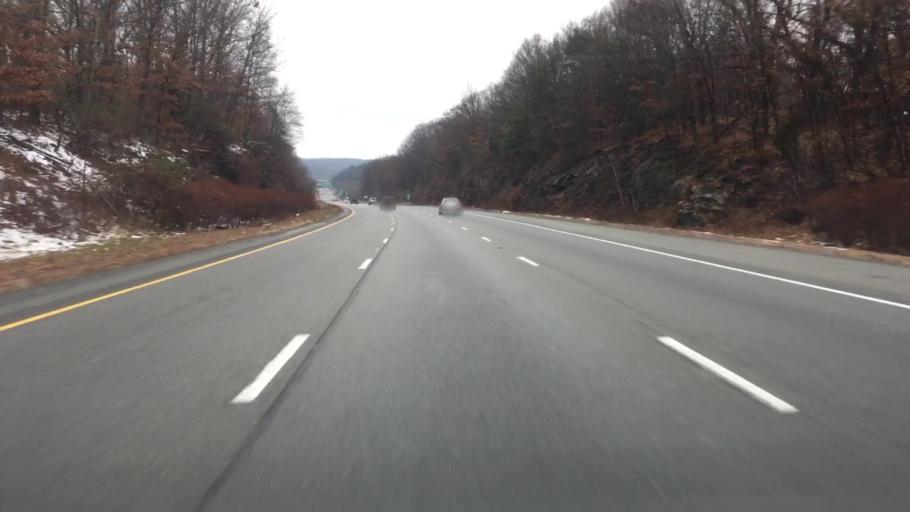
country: US
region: Massachusetts
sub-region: Middlesex County
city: Marlborough
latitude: 42.3514
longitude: -71.5775
